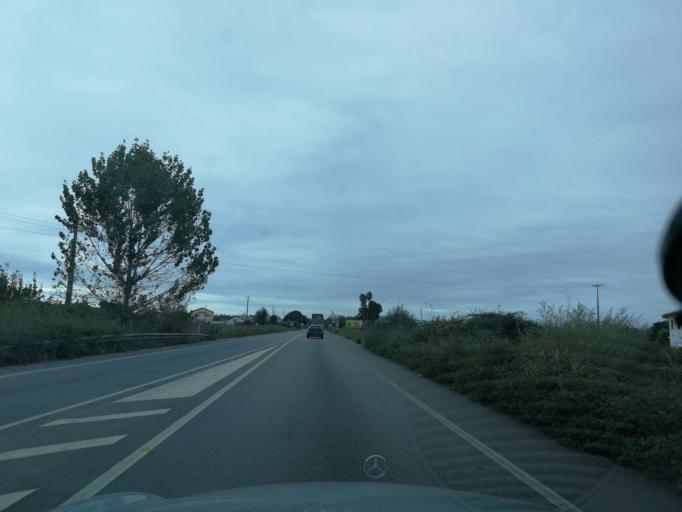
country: PT
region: Aveiro
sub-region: Agueda
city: Valongo
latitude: 40.6169
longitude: -8.4632
